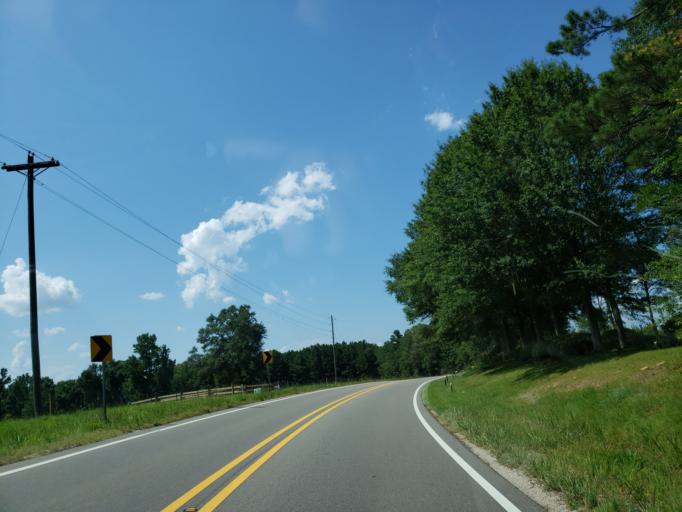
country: US
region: Mississippi
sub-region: Lamar County
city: Sumrall
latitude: 31.3696
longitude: -89.5091
